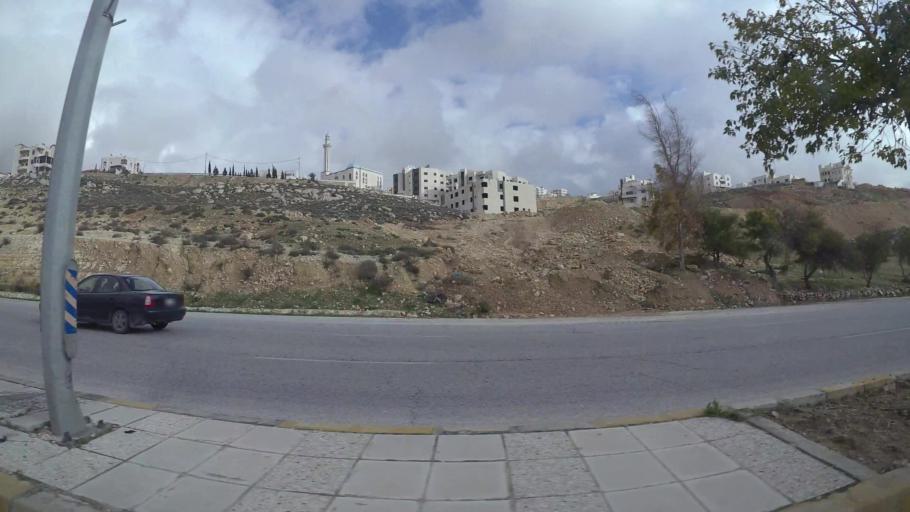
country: JO
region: Amman
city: Al Jubayhah
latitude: 32.0701
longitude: 35.8747
